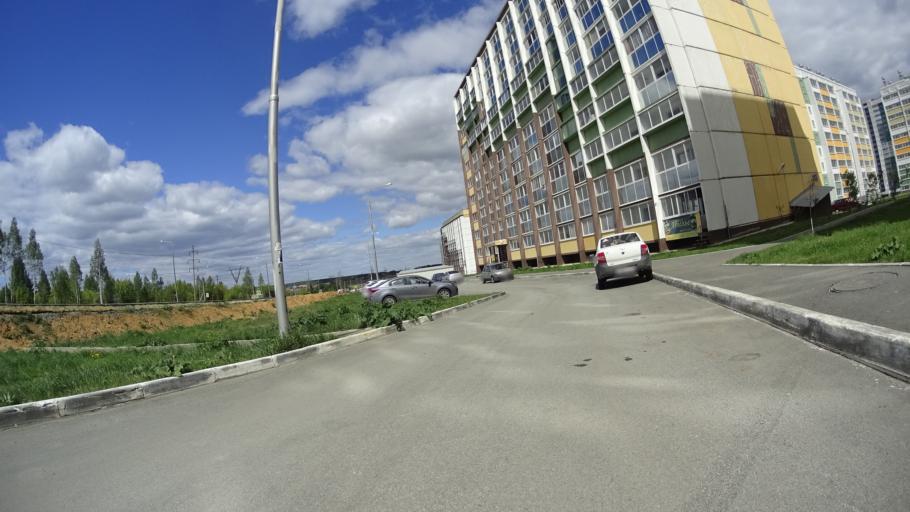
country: RU
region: Chelyabinsk
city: Roshchino
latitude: 55.1736
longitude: 61.2562
